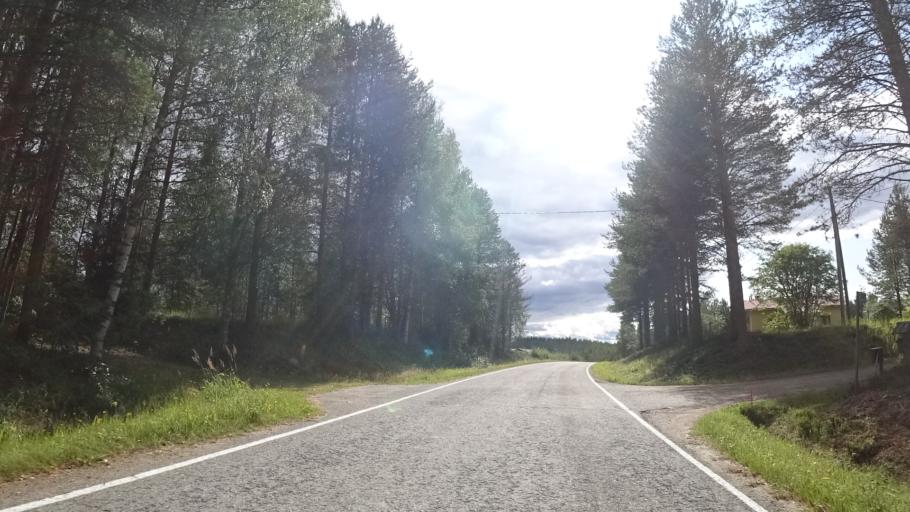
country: FI
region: North Karelia
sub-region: Joensuu
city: Ilomantsi
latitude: 62.4462
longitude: 31.1134
